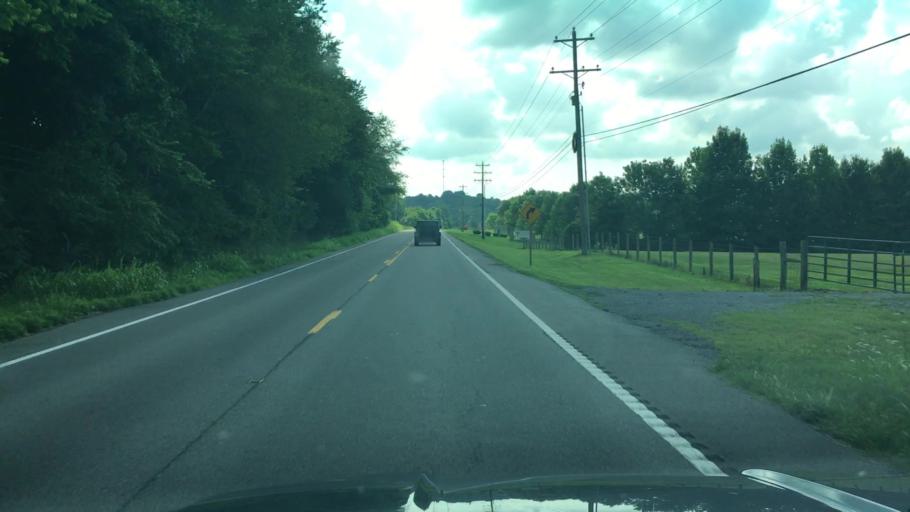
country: US
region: Tennessee
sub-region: Williamson County
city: Nolensville
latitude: 35.8584
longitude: -86.6750
